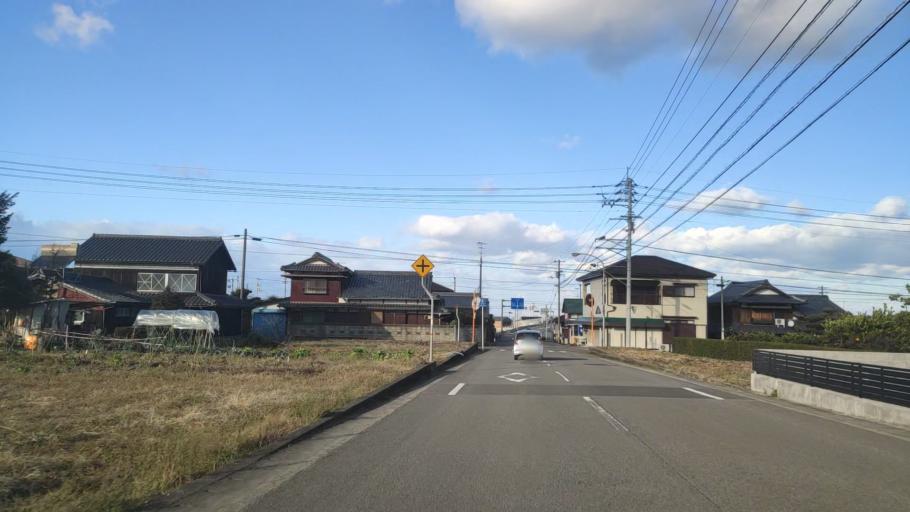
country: JP
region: Ehime
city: Saijo
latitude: 33.8939
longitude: 133.1322
